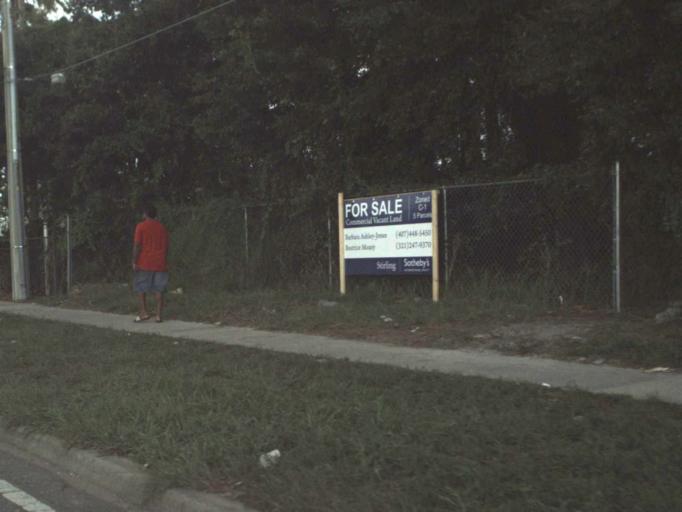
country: US
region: Florida
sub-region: Orange County
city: Orlando
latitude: 28.5471
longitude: -81.4136
